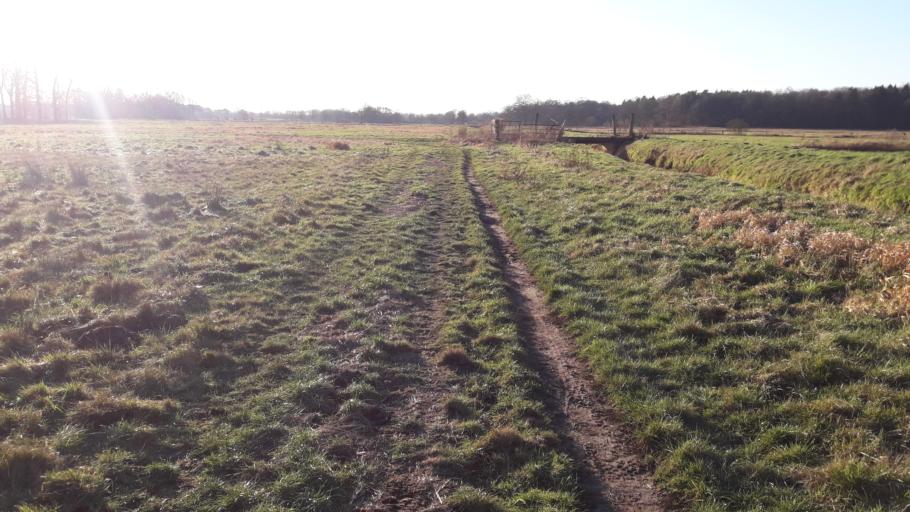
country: DE
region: Schleswig-Holstein
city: Hasloh
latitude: 53.7129
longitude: 9.8644
